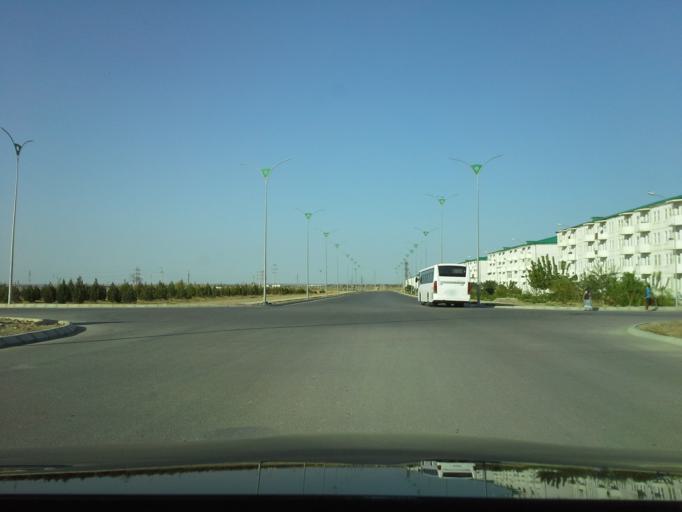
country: TM
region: Ahal
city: Abadan
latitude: 38.0540
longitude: 58.1376
